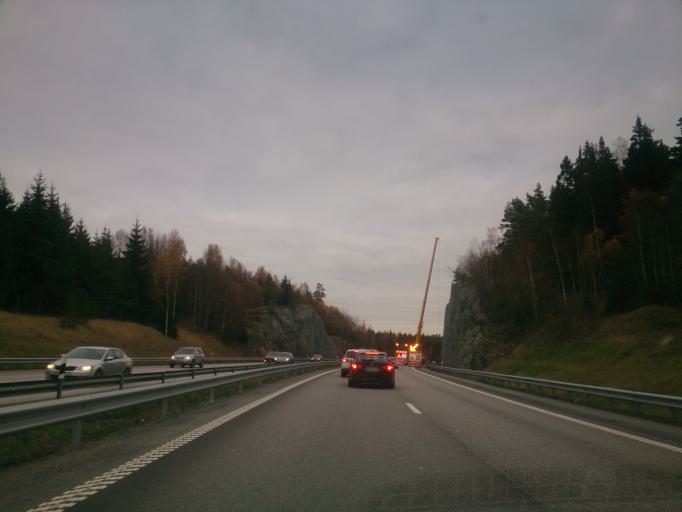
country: SE
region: Stockholm
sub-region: Sodertalje Kommun
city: Pershagen
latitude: 59.1116
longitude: 17.6103
